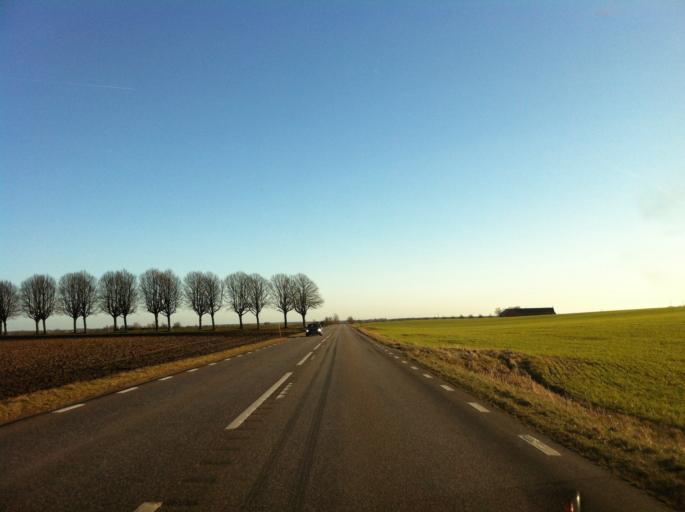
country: SE
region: Skane
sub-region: Landskrona
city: Asmundtorp
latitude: 55.9112
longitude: 12.9570
